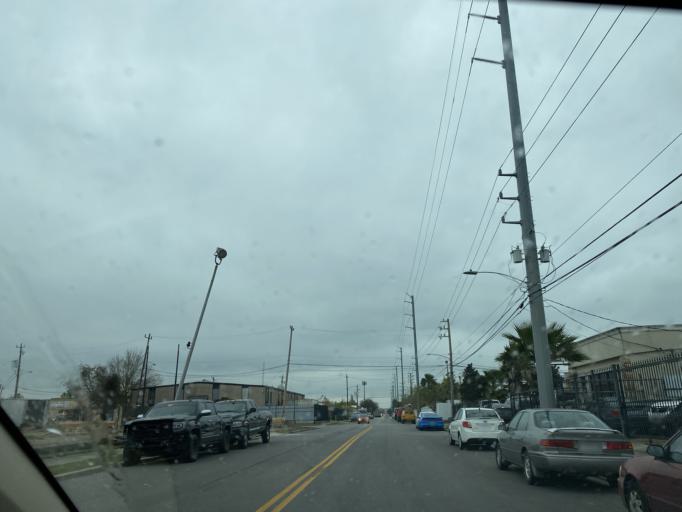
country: US
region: Texas
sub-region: Harris County
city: Piney Point Village
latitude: 29.7269
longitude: -95.5194
